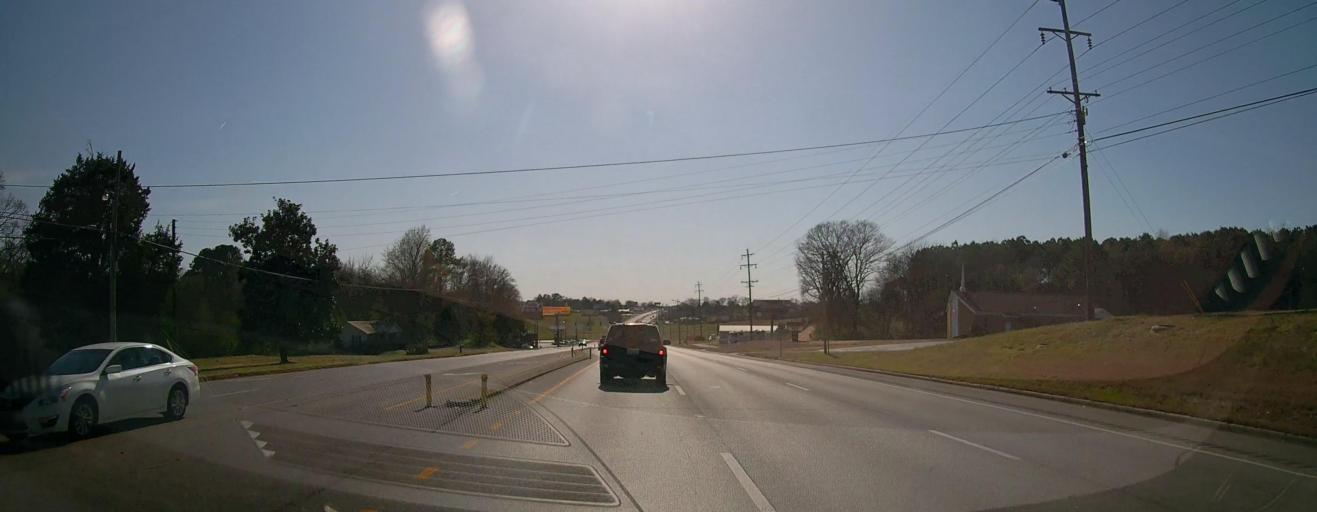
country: US
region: Alabama
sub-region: Lauderdale County
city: East Florence
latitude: 34.8363
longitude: -87.6073
